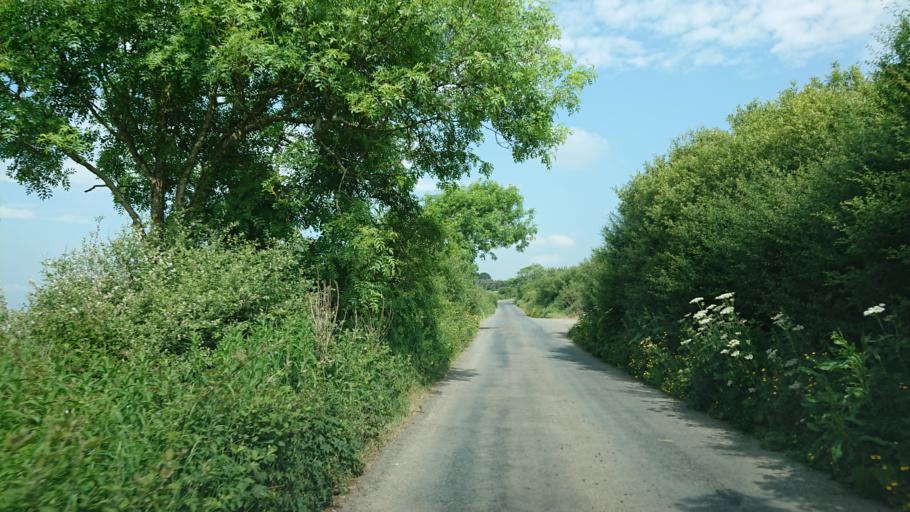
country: IE
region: Munster
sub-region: Waterford
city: Dunmore East
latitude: 52.2250
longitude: -7.0060
